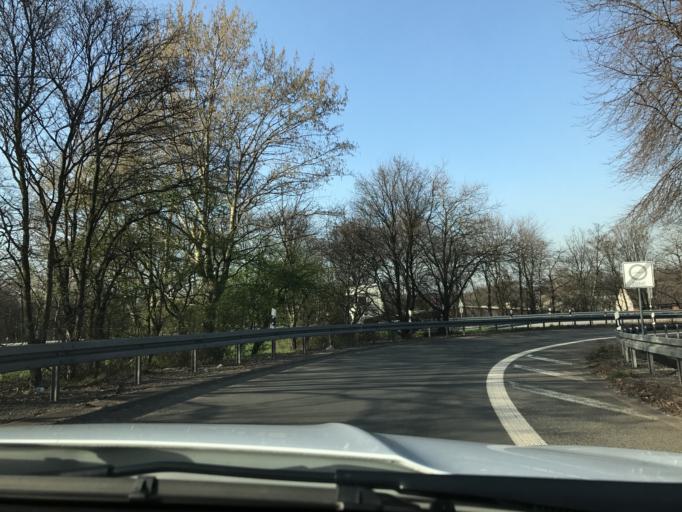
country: DE
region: North Rhine-Westphalia
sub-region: Regierungsbezirk Dusseldorf
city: Duisburg
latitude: 51.4361
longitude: 6.7496
